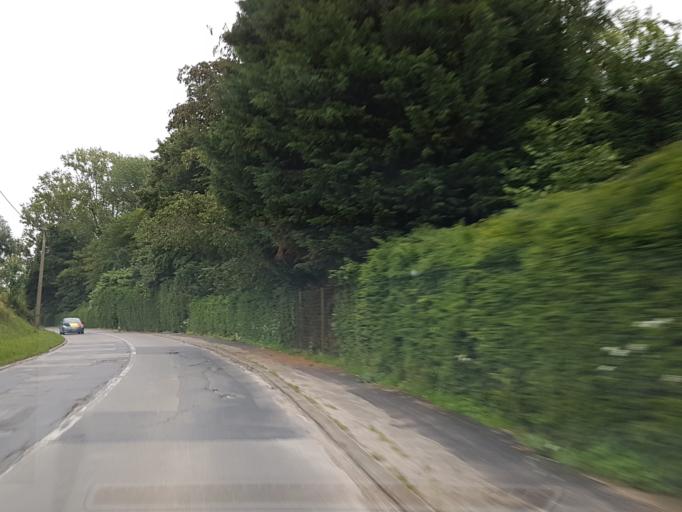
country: BE
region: Flanders
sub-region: Provincie Vlaams-Brabant
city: Wemmel
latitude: 50.9364
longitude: 4.2824
